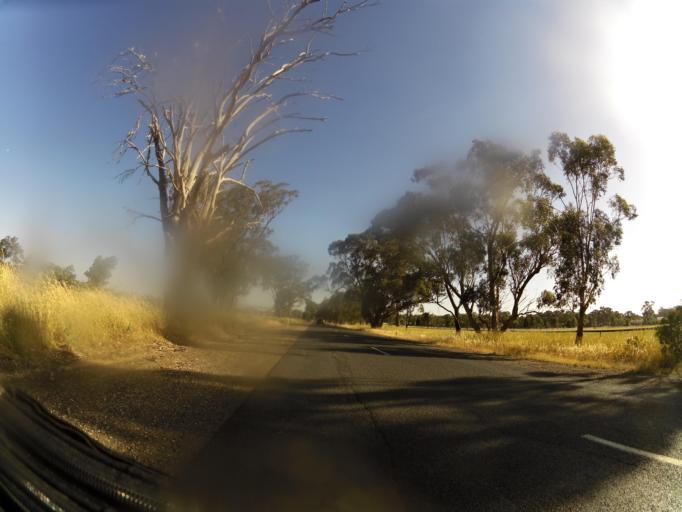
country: AU
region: Victoria
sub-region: Murrindindi
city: Kinglake West
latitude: -36.9824
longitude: 145.1110
